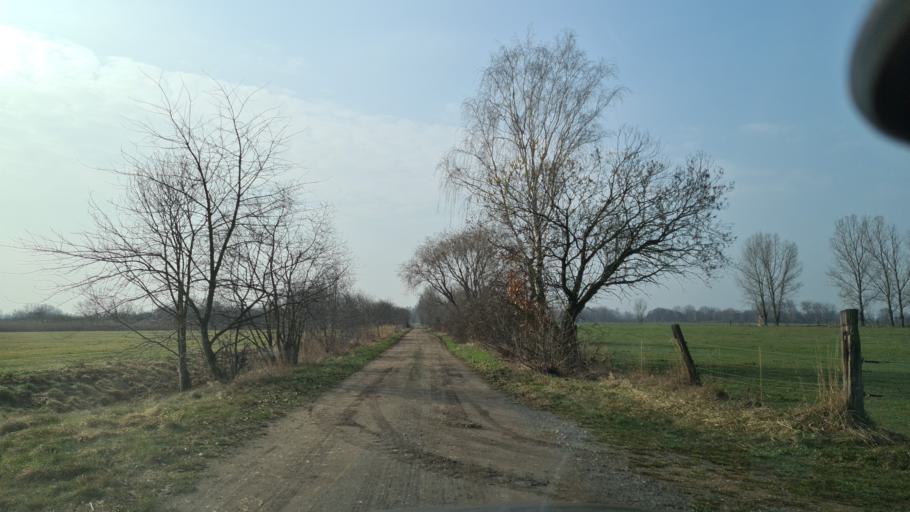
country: DE
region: Brandenburg
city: Bad Liebenwerda
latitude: 51.5371
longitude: 13.3619
